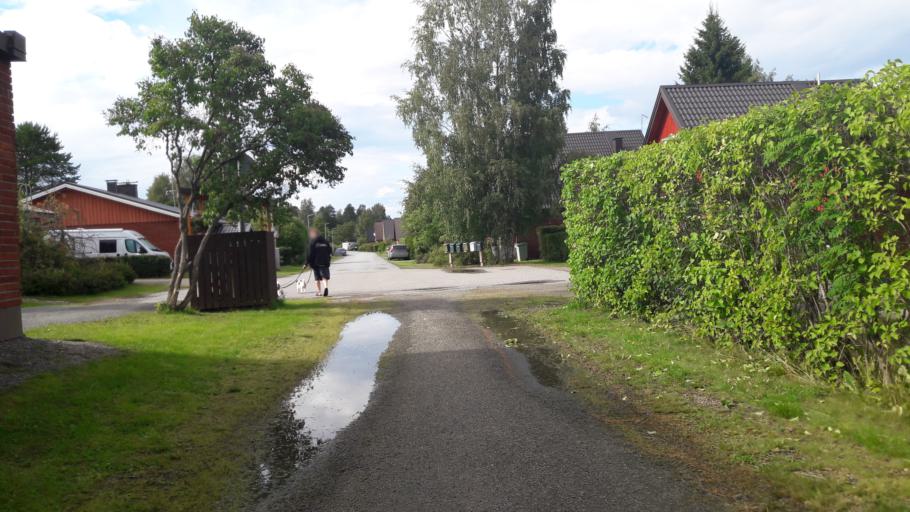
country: FI
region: North Karelia
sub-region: Joensuu
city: Joensuu
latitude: 62.5793
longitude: 29.8118
